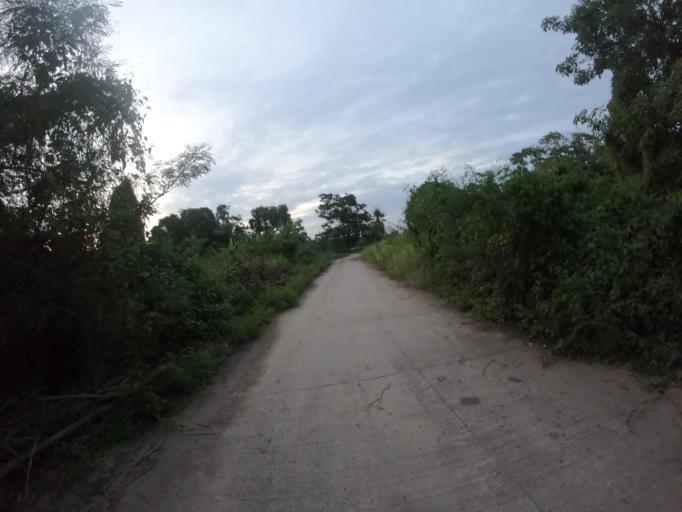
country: TH
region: Pathum Thani
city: Ban Rangsit
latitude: 14.0225
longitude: 100.8018
